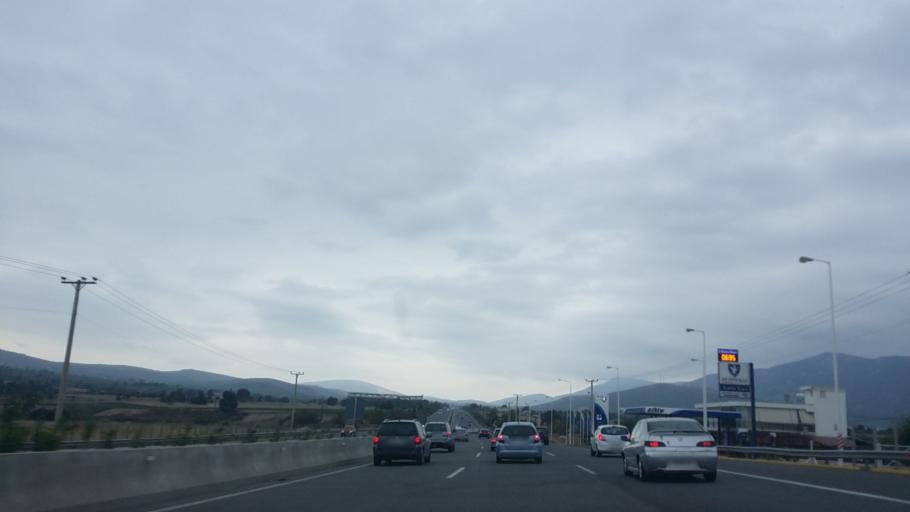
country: GR
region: Attica
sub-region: Nomarchia Anatolikis Attikis
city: Avlonas
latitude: 38.2704
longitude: 23.6973
